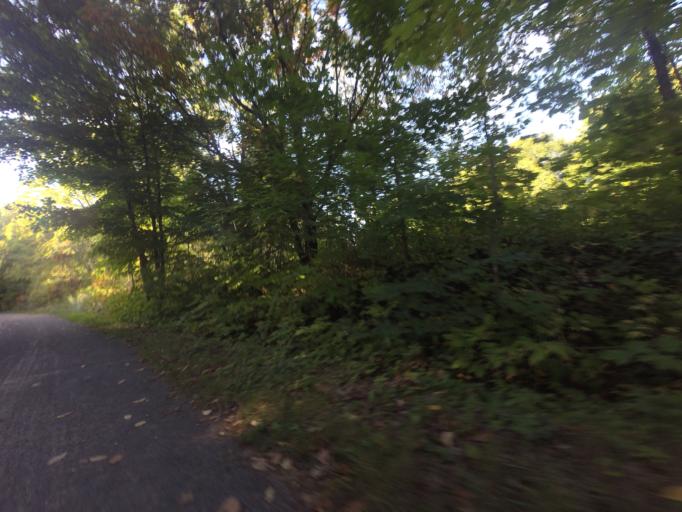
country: CA
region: Quebec
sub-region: Laurentides
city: Saint-Jerome
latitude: 45.8112
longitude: -74.0215
